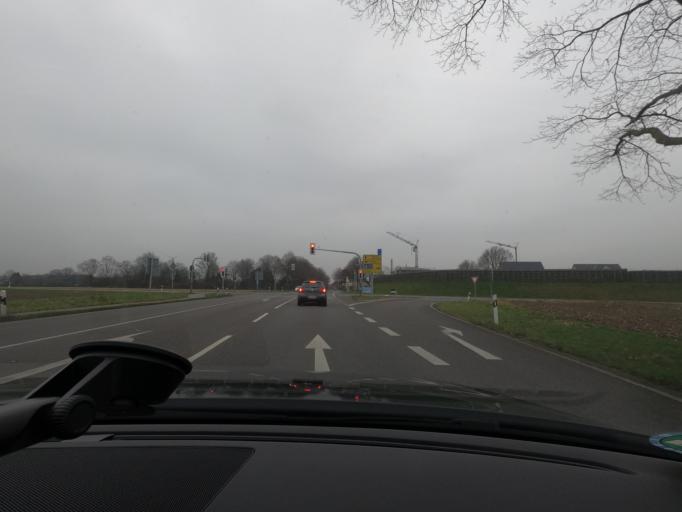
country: DE
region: North Rhine-Westphalia
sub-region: Regierungsbezirk Dusseldorf
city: Wachtendonk
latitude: 51.3999
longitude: 6.2992
